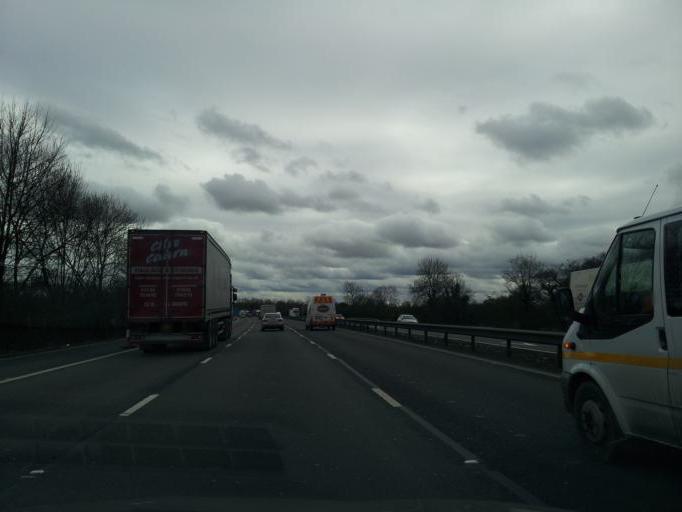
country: GB
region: England
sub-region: Staffordshire
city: Stone
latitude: 52.9027
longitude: -2.1895
